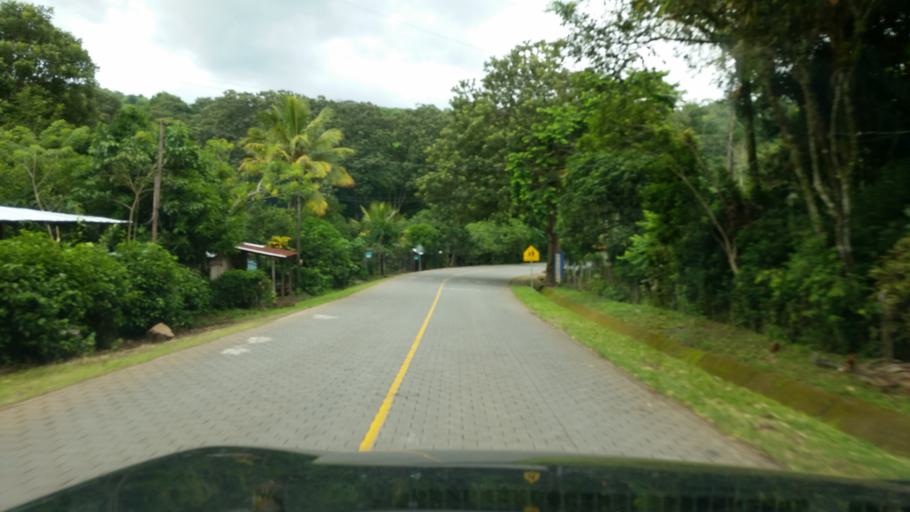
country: NI
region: Jinotega
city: Jinotega
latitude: 13.2058
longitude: -85.7244
